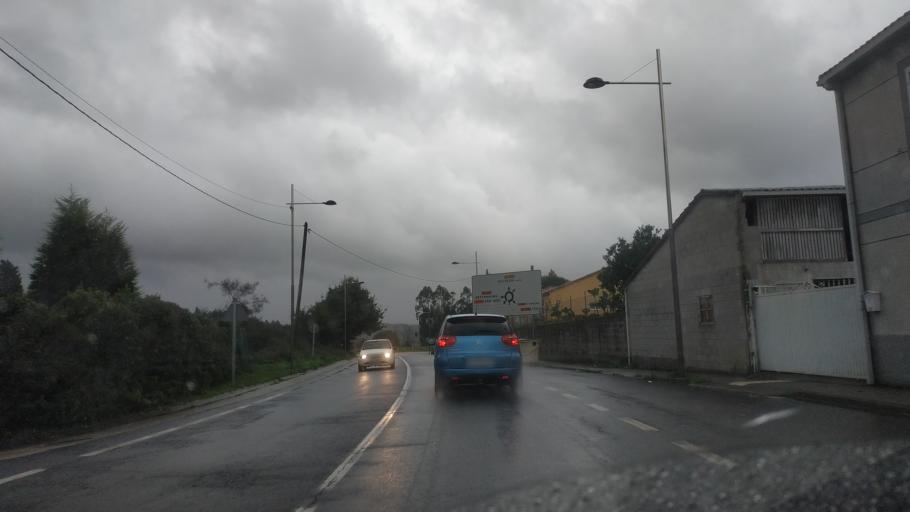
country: ES
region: Galicia
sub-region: Provincia da Coruna
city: Negreira
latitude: 42.9219
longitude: -8.7345
